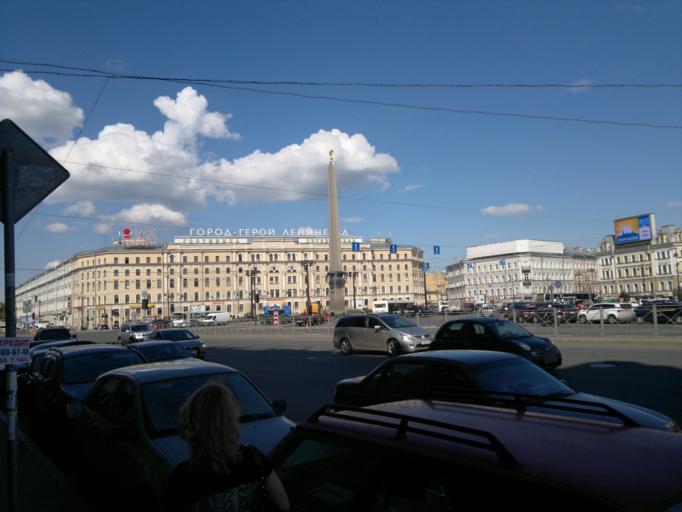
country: RU
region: St.-Petersburg
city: Centralniy
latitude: 59.9303
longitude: 30.3602
